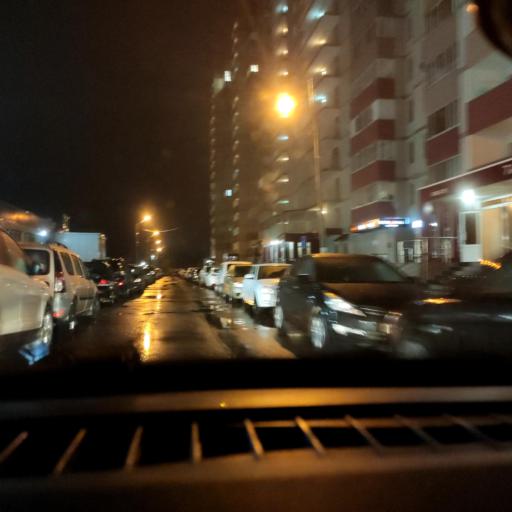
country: RU
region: Voronezj
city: Voronezh
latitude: 51.7121
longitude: 39.2009
